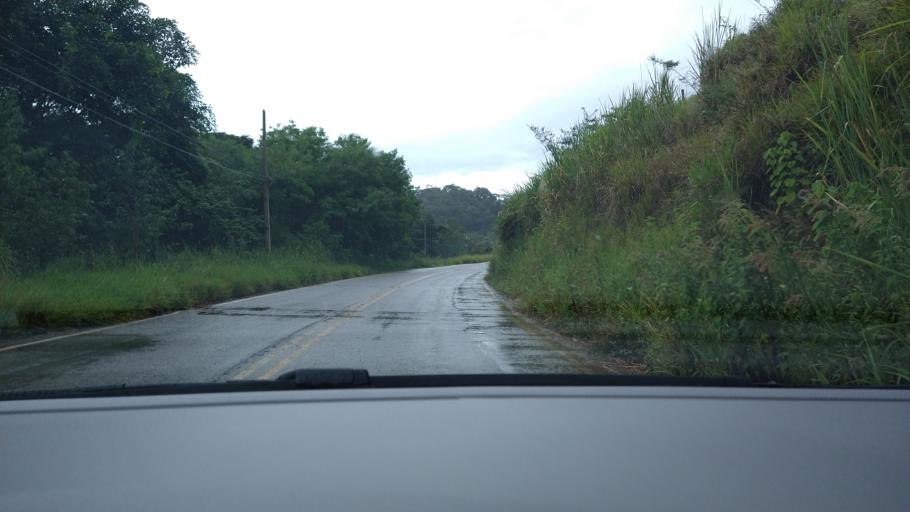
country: BR
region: Minas Gerais
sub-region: Ponte Nova
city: Ponte Nova
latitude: -20.3813
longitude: -42.9023
